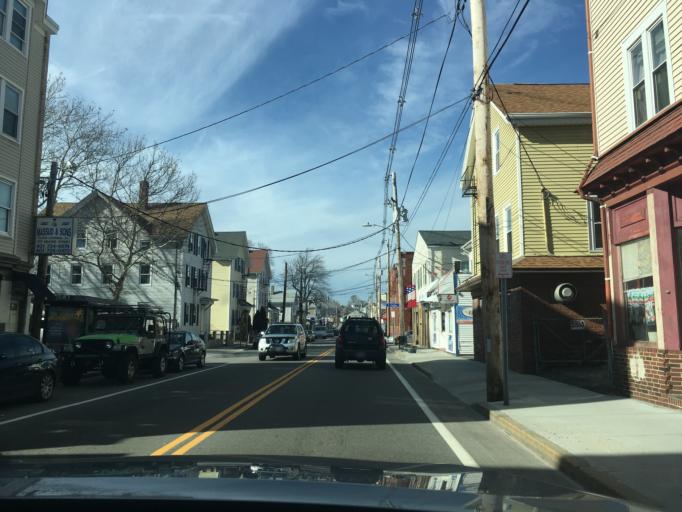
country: US
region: Rhode Island
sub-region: Providence County
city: Central Falls
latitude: 41.8874
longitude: -71.3976
